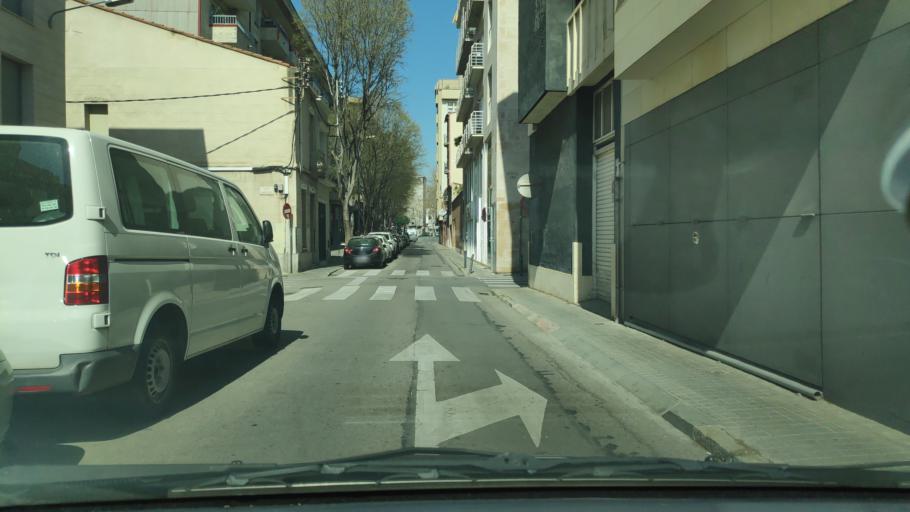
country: ES
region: Catalonia
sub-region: Provincia de Barcelona
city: Sabadell
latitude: 41.5499
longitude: 2.1045
